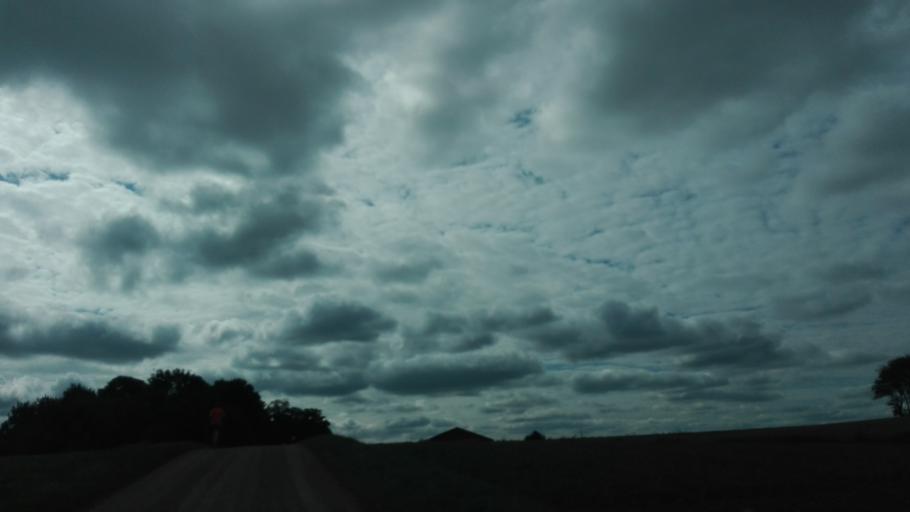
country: DK
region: Central Jutland
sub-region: Skanderborg Kommune
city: Stilling
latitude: 56.0839
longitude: 10.0003
